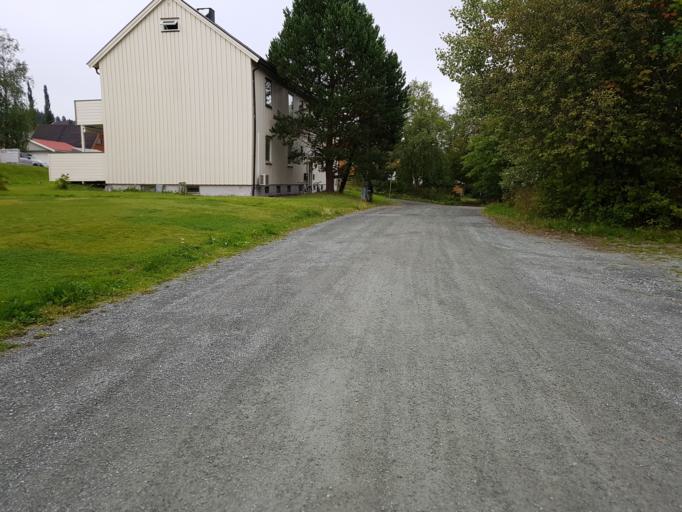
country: NO
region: Sor-Trondelag
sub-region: Trondheim
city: Trondheim
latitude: 63.3974
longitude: 10.3656
